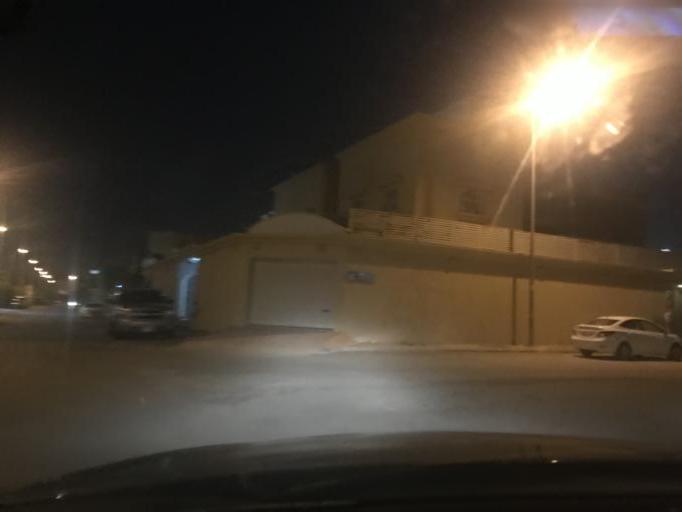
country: SA
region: Ar Riyad
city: Riyadh
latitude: 24.7499
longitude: 46.7513
